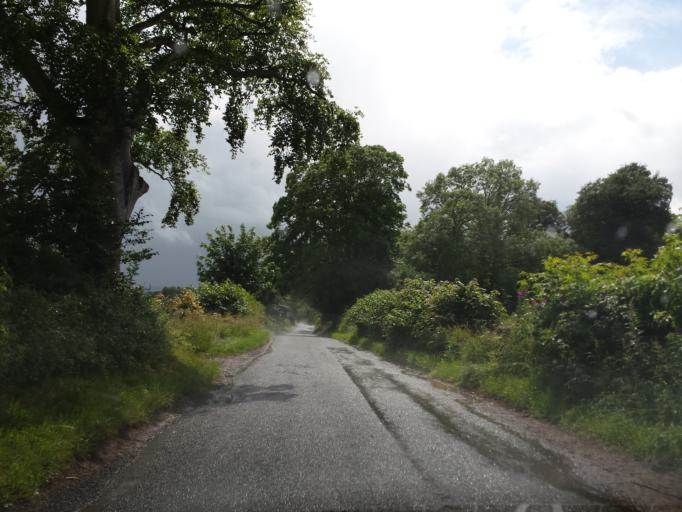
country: GB
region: Scotland
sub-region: The Scottish Borders
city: Saint Boswells
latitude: 55.5886
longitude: -2.6438
